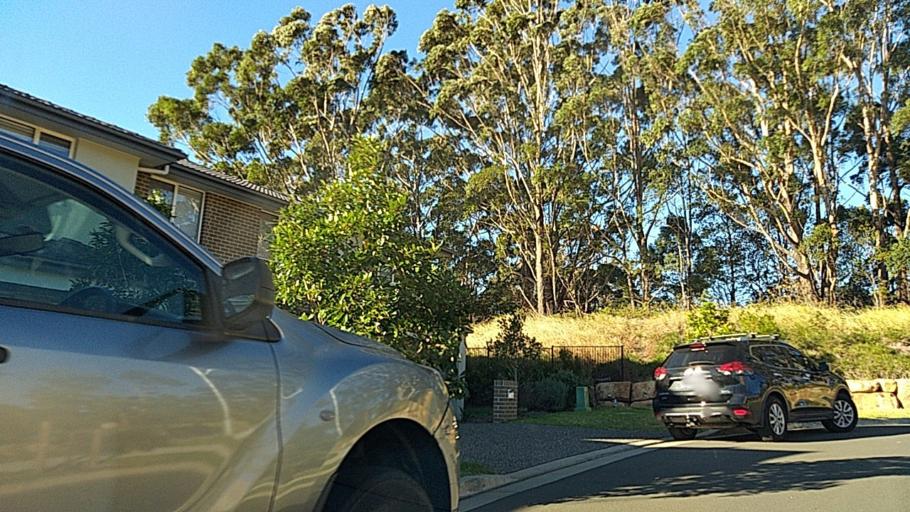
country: AU
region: New South Wales
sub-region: Wollongong
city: Bulli
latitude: -34.3337
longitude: 150.9102
